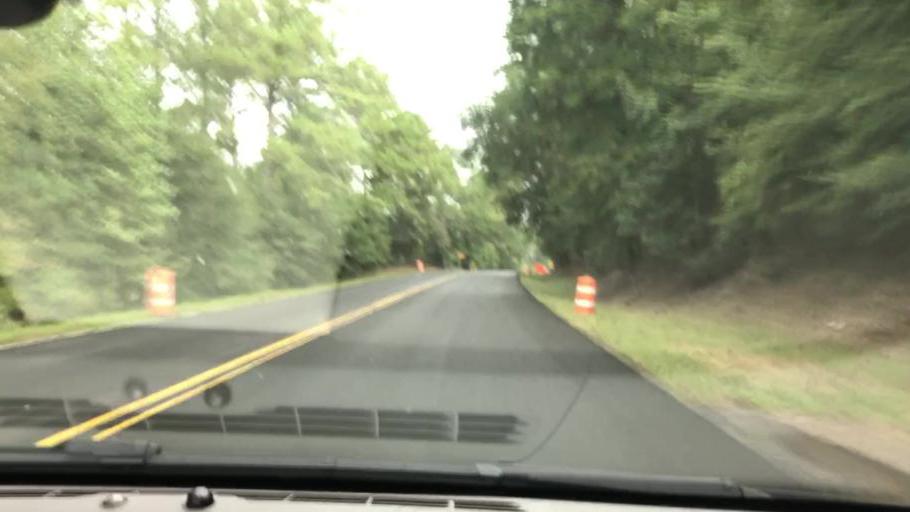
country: US
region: Georgia
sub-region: Clay County
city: Fort Gaines
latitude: 31.5168
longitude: -85.0236
